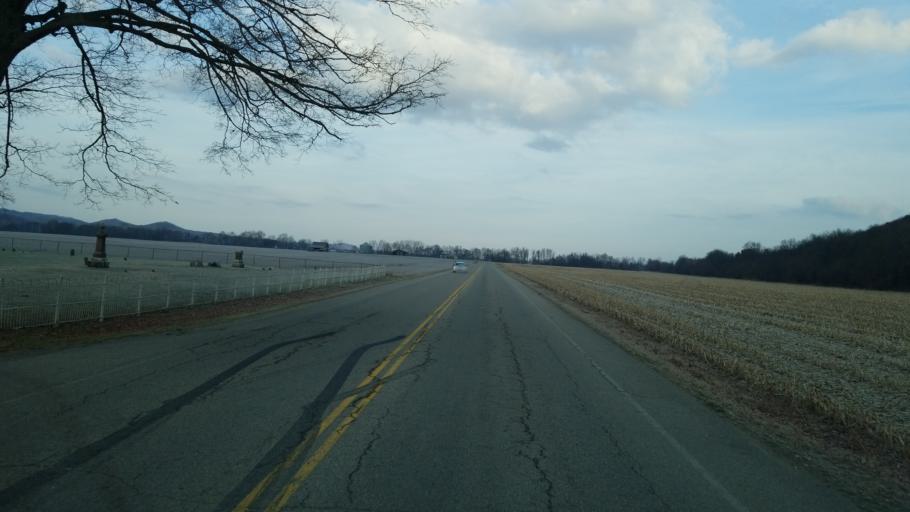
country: US
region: Ohio
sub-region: Pike County
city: Waverly
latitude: 39.2221
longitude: -82.8494
